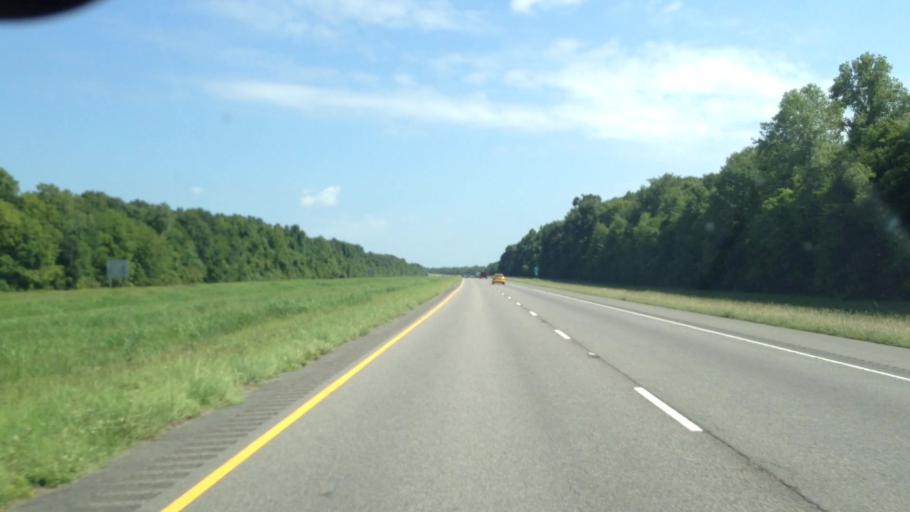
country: US
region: Louisiana
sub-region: Avoyelles Parish
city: Bunkie
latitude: 30.8808
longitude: -92.2271
